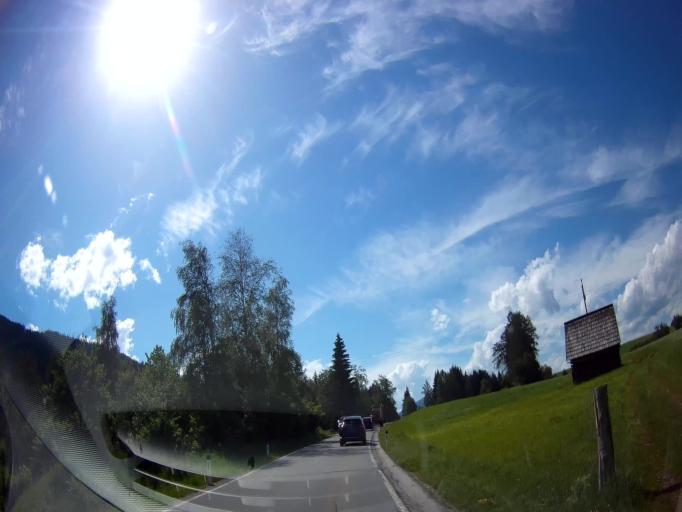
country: AT
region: Salzburg
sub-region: Politischer Bezirk Tamsweg
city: Thomatal
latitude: 47.0798
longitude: 13.7285
